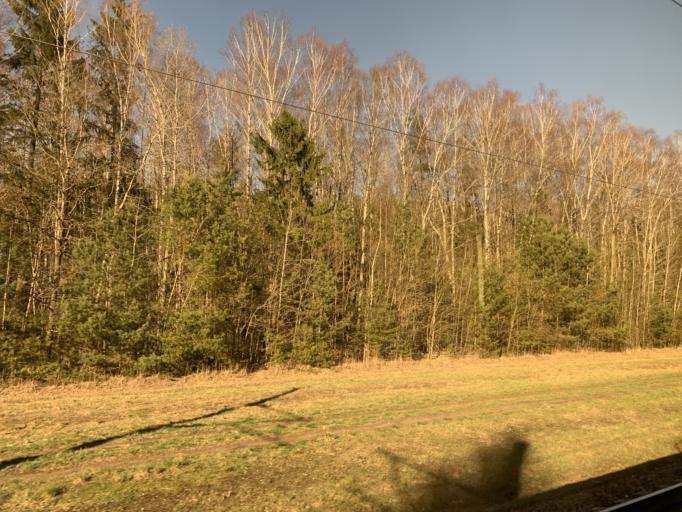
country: BY
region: Grodnenskaya
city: Smarhon'
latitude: 54.4899
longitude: 26.2991
